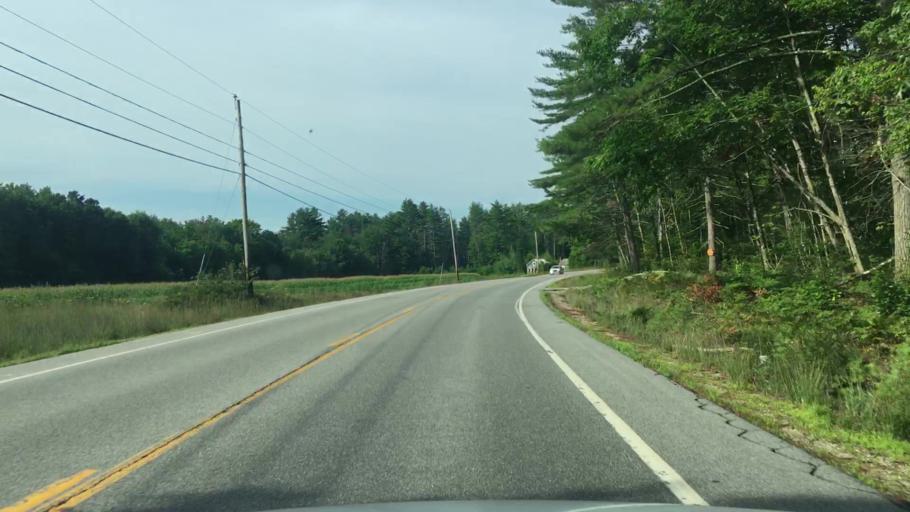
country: US
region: Maine
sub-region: Oxford County
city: Porter
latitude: 43.7906
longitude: -70.9505
